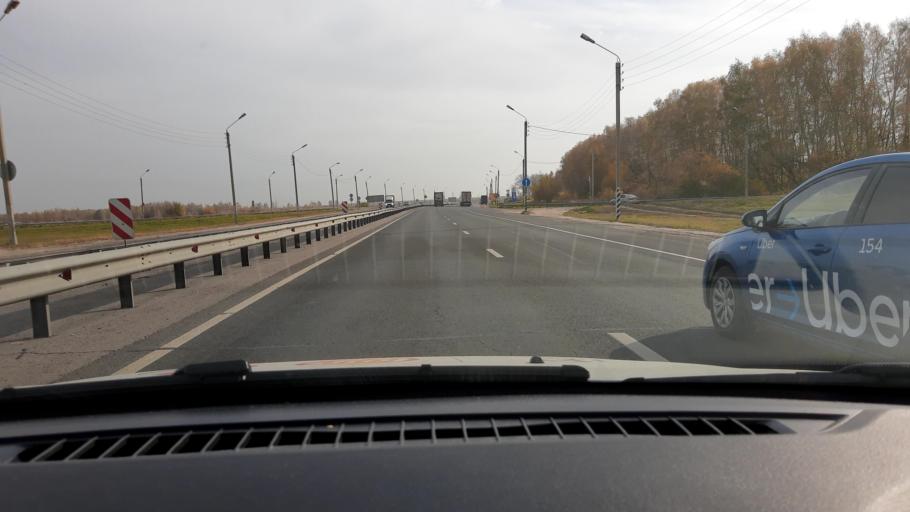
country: RU
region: Nizjnij Novgorod
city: Kstovo
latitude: 56.1267
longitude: 44.2628
